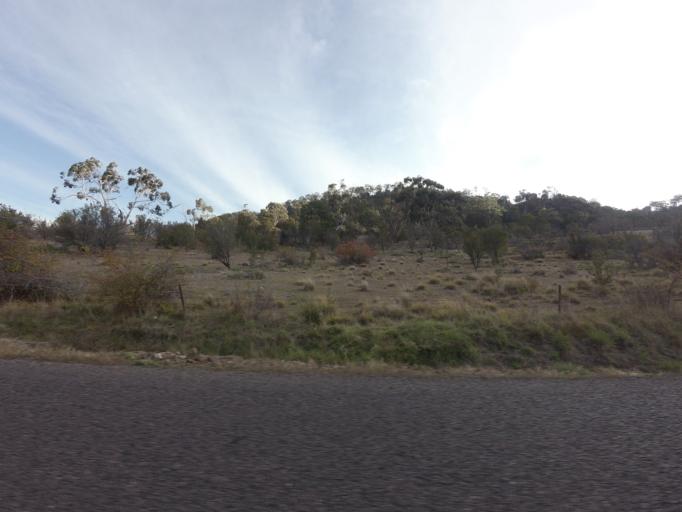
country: AU
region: Tasmania
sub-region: Brighton
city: Bridgewater
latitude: -42.4273
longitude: 147.1414
